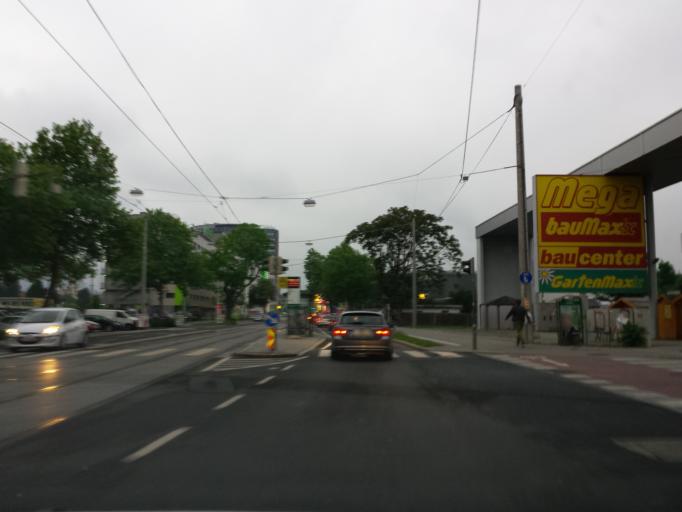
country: AT
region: Styria
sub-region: Graz Stadt
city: Graz
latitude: 47.0538
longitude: 15.4490
